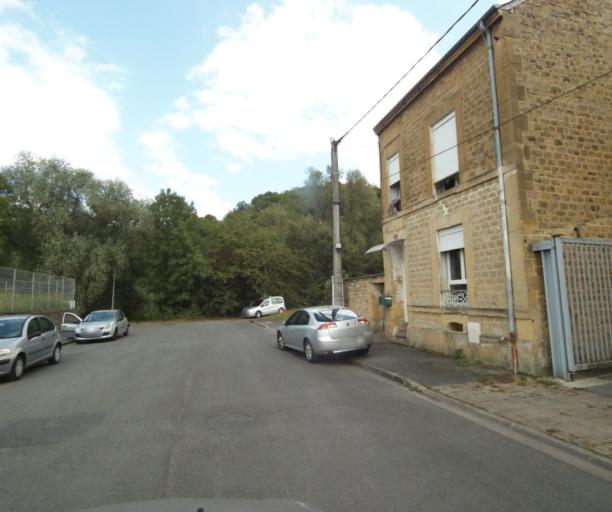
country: FR
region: Champagne-Ardenne
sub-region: Departement des Ardennes
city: Montcy-Notre-Dame
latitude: 49.7708
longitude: 4.7328
